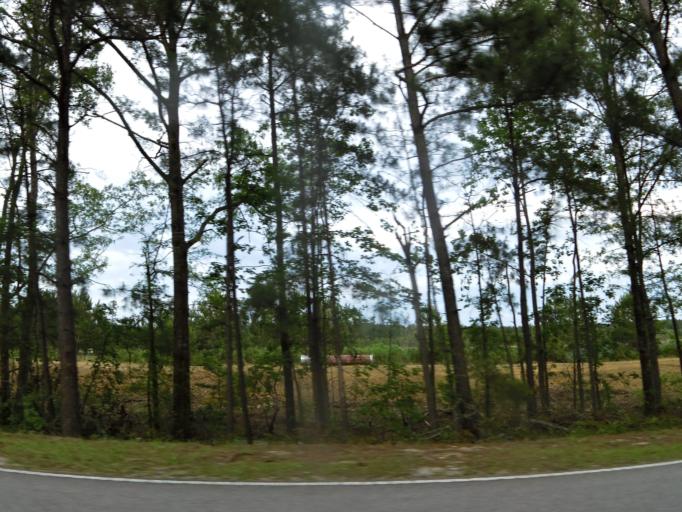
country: US
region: South Carolina
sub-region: Jasper County
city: Hardeeville
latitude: 32.3948
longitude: -81.0987
